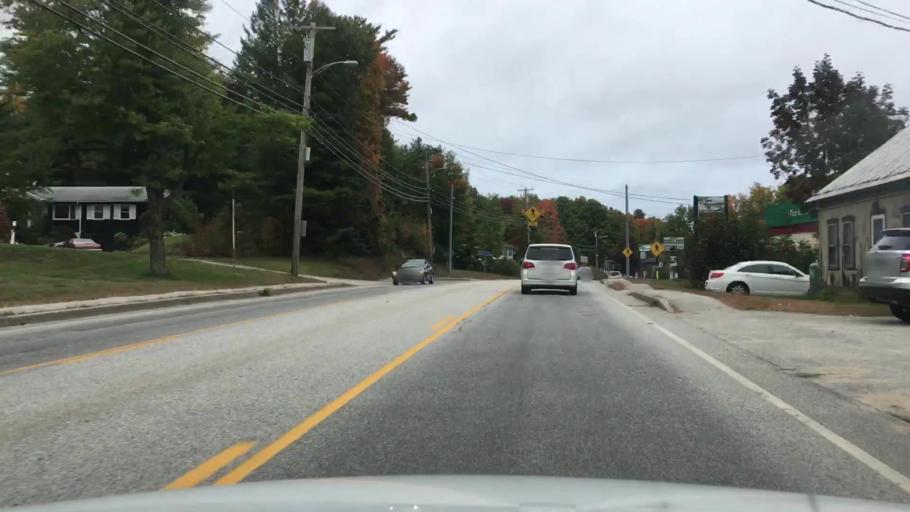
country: US
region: Maine
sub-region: Oxford County
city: Norway
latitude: 44.2007
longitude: -70.5299
